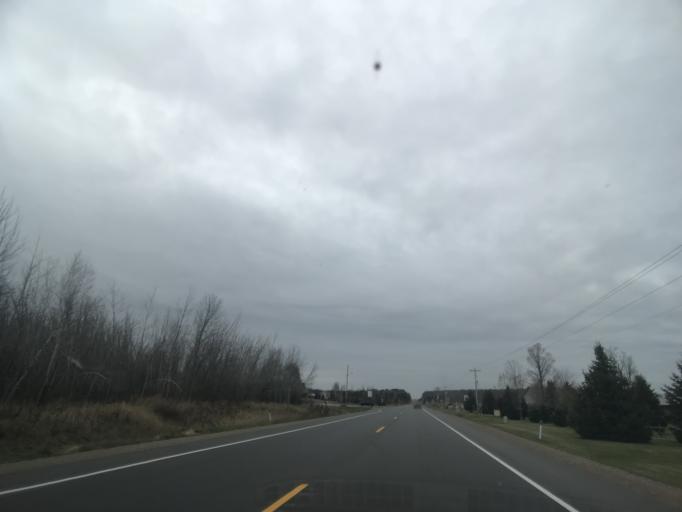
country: US
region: Wisconsin
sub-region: Menominee County
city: Legend Lake
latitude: 45.2353
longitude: -88.5158
